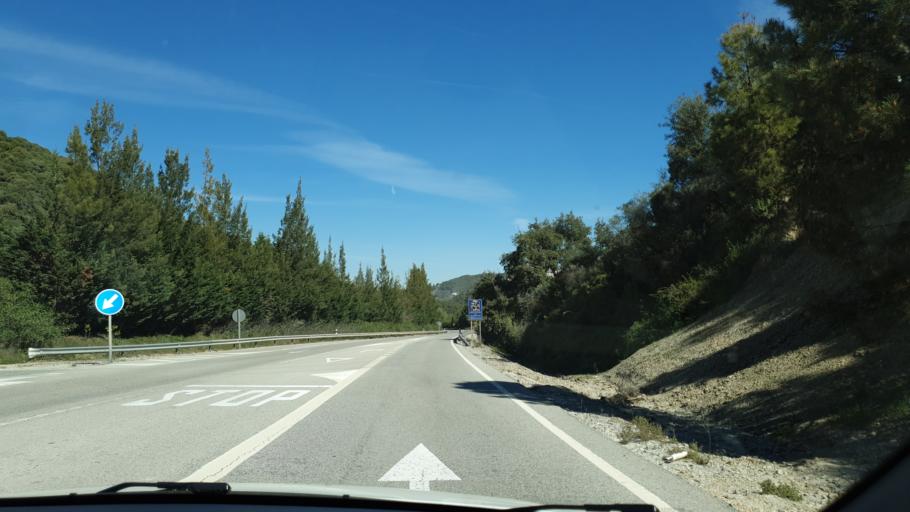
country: ES
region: Andalusia
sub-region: Provincia de Malaga
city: Ojen
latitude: 36.5856
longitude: -4.8526
